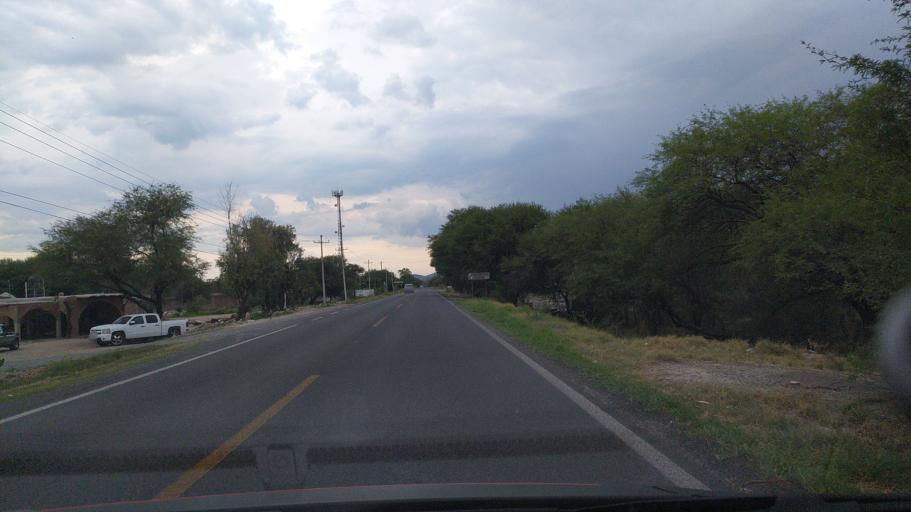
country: MX
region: Guanajuato
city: San Roque
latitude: 20.9727
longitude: -101.8565
